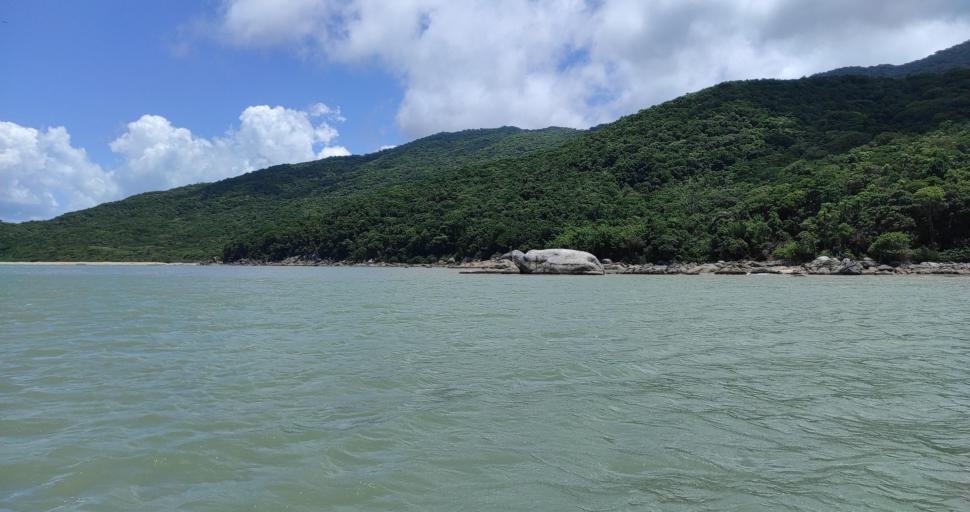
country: BR
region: Santa Catarina
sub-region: Porto Belo
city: Porto Belo
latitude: -27.2006
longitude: -48.5617
